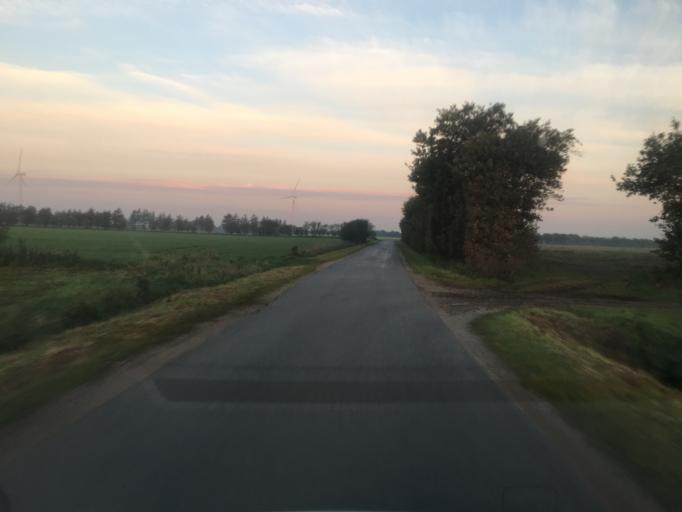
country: DK
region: South Denmark
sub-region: Tonder Kommune
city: Logumkloster
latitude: 54.9856
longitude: 9.0564
